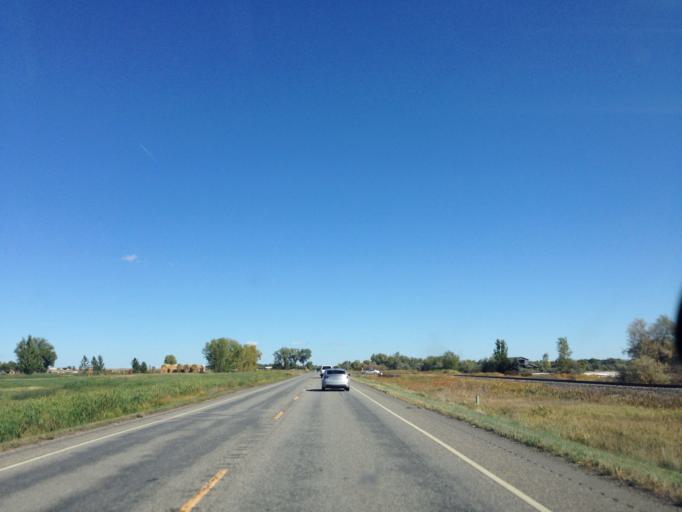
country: US
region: Montana
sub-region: Yellowstone County
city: Laurel
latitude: 45.5981
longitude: -108.8089
